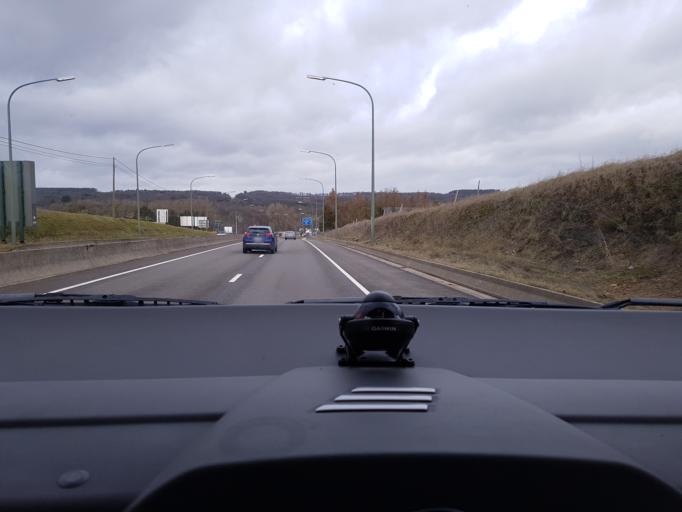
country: BE
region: Wallonia
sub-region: Province du Luxembourg
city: Marche-en-Famenne
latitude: 50.2446
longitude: 5.2873
